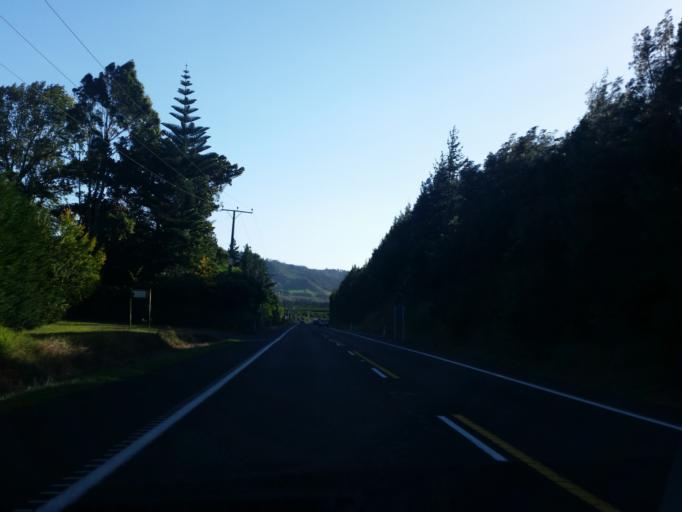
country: NZ
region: Bay of Plenty
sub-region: Western Bay of Plenty District
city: Katikati
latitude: -37.5178
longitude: 175.9194
